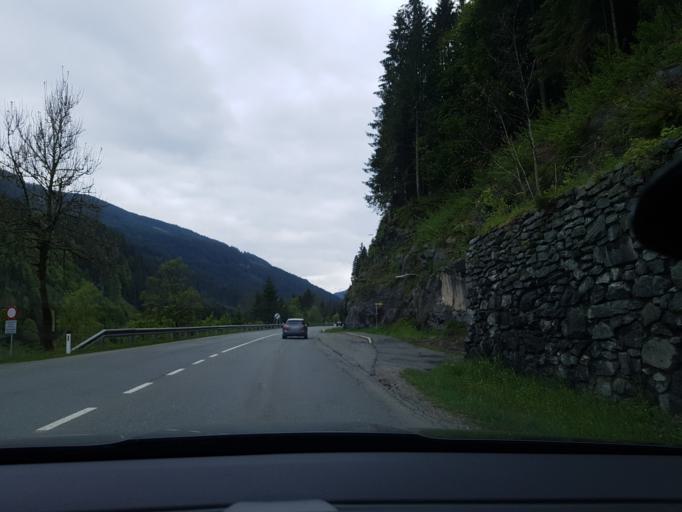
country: AT
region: Tyrol
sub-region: Politischer Bezirk Kitzbuhel
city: Jochberg
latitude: 47.3546
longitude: 12.4142
